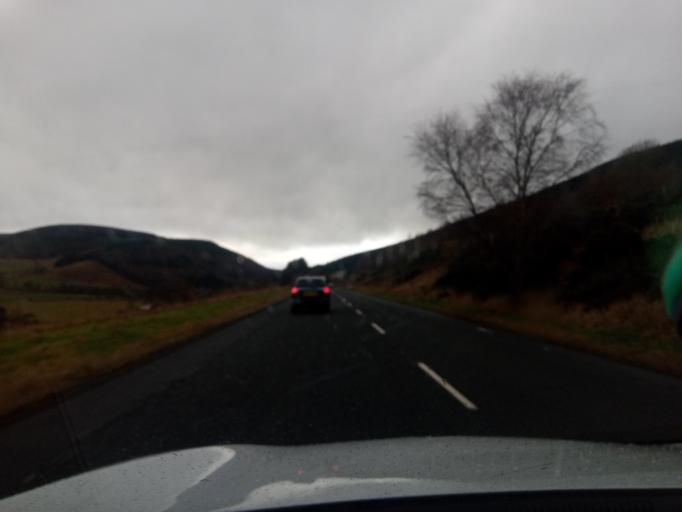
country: GB
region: Scotland
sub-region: The Scottish Borders
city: Innerleithen
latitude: 55.6292
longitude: -2.9965
